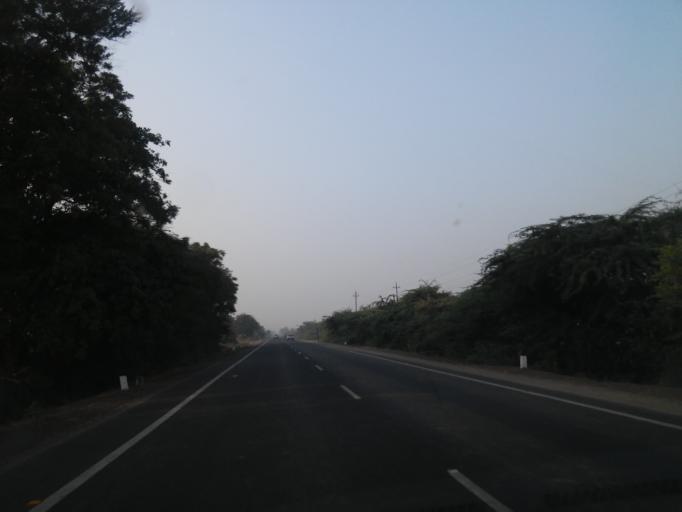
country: IN
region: Gujarat
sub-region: Kachchh
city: Mandvi
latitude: 22.8568
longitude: 69.3833
